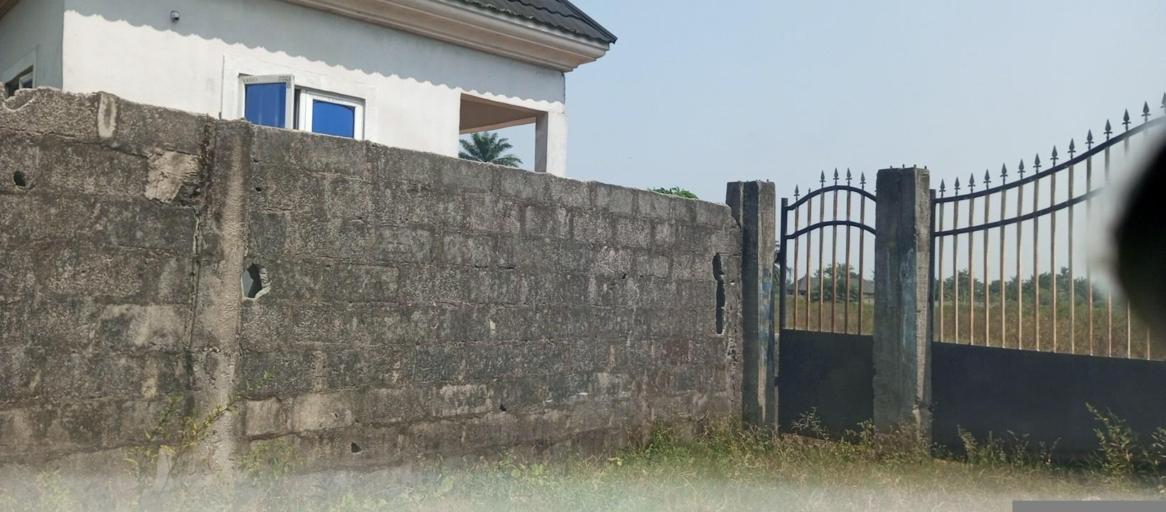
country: NG
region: Rivers
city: Emuoha
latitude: 4.9176
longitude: 6.9210
